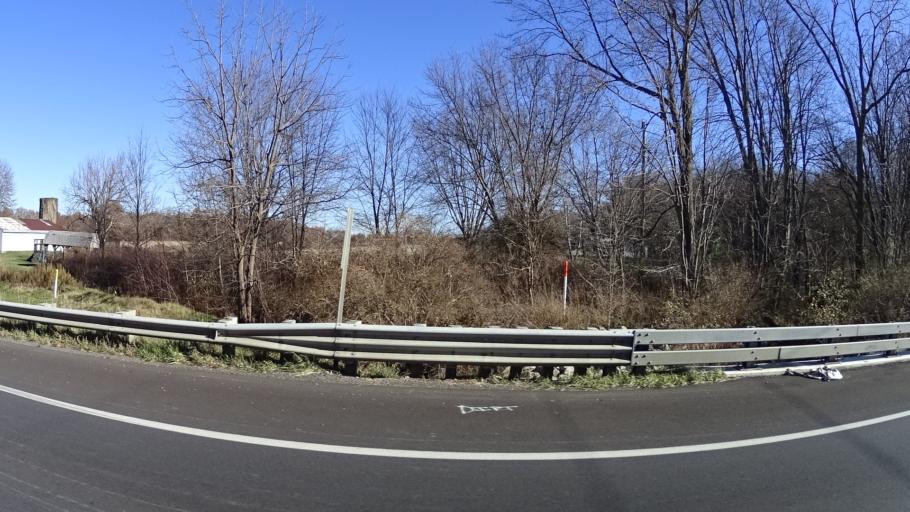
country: US
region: Ohio
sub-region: Lorain County
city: Lagrange
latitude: 41.2784
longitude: -82.1183
